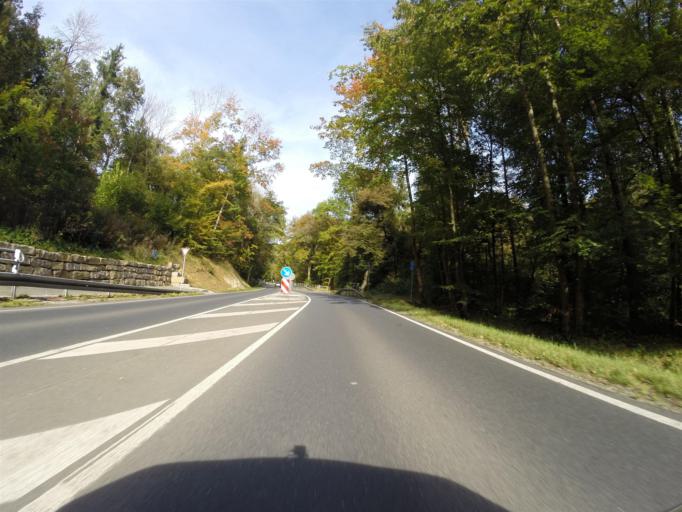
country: DE
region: Thuringia
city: Grossschwabhausen
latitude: 50.9499
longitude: 11.5358
